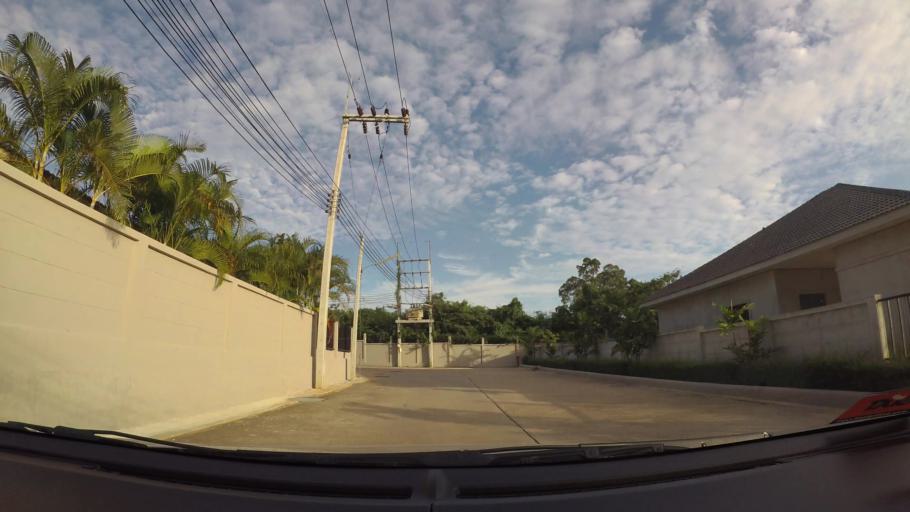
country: TH
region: Chon Buri
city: Sattahip
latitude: 12.7262
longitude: 100.9168
